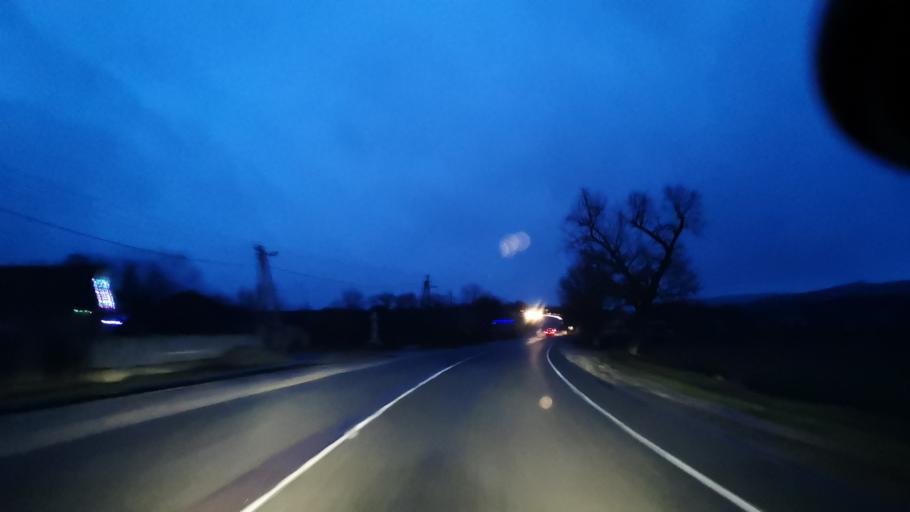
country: MD
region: Orhei
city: Orhei
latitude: 47.4588
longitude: 28.7902
